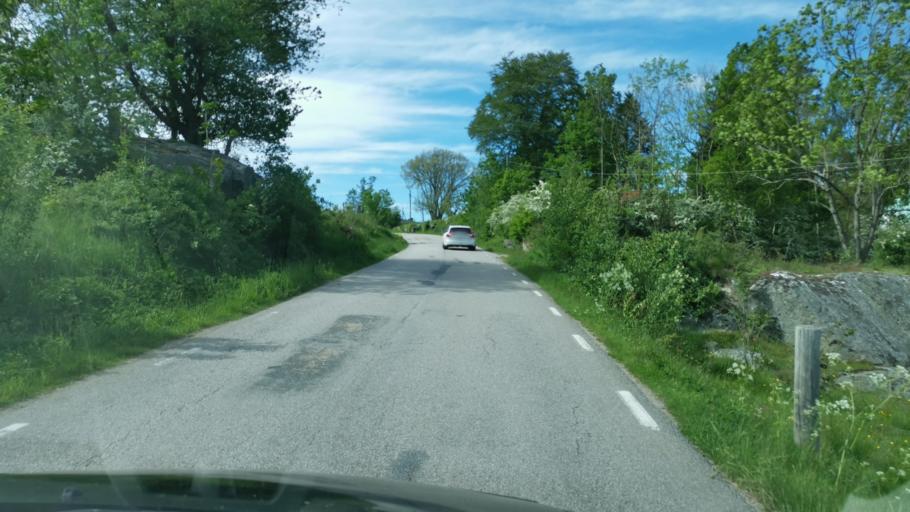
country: SE
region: Vaestra Goetaland
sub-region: Orust
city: Henan
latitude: 58.2714
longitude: 11.6004
